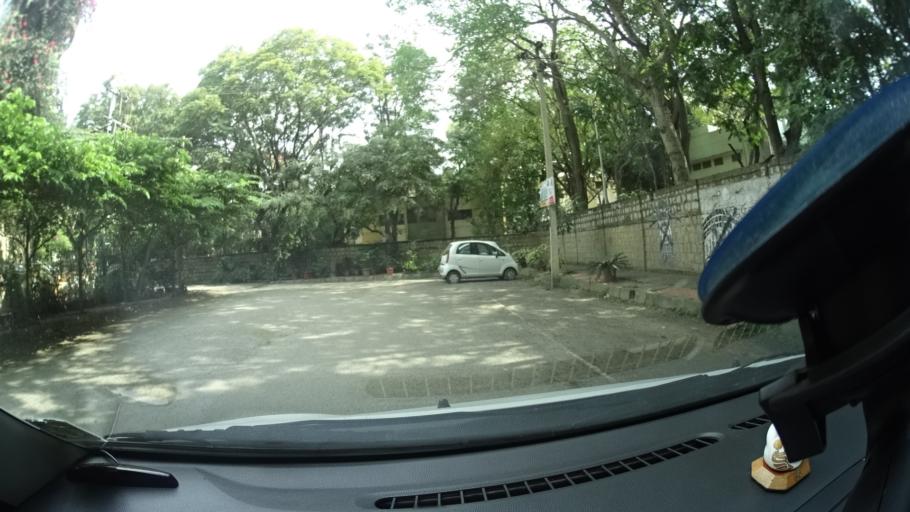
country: IN
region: Karnataka
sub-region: Bangalore Urban
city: Yelahanka
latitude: 13.1031
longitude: 77.5806
